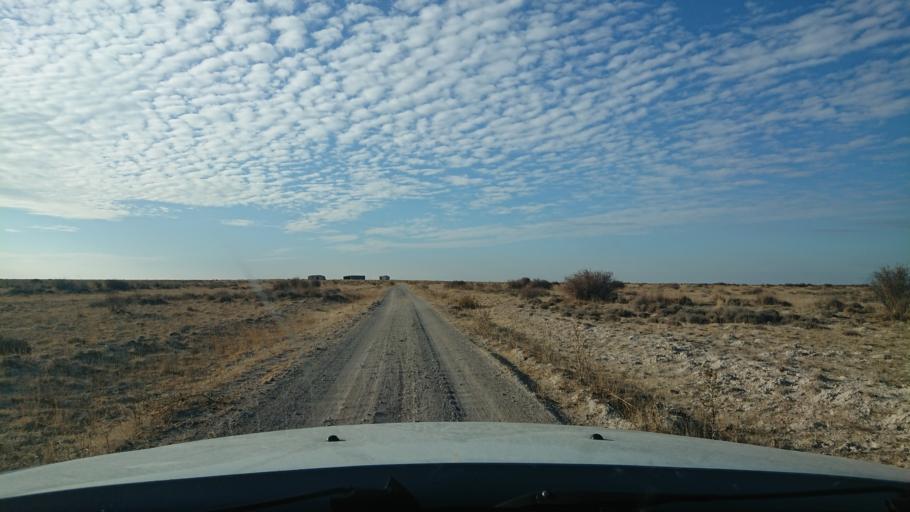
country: TR
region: Aksaray
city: Eskil
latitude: 38.5447
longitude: 33.3238
